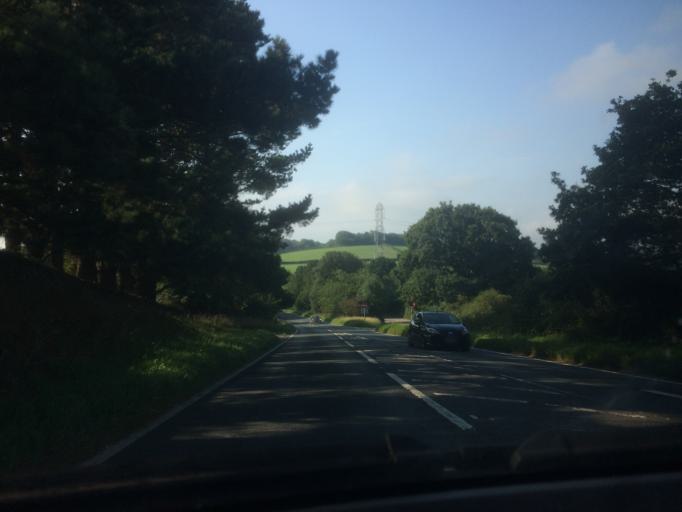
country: GB
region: England
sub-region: Cornwall
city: Pillaton
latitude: 50.4469
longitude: -4.2558
